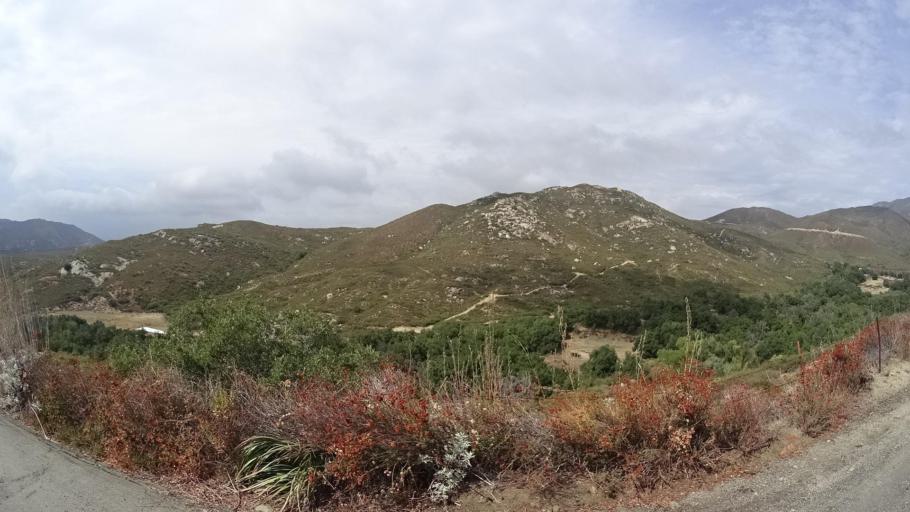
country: US
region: California
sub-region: San Diego County
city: Descanso
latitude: 32.9156
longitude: -116.6384
